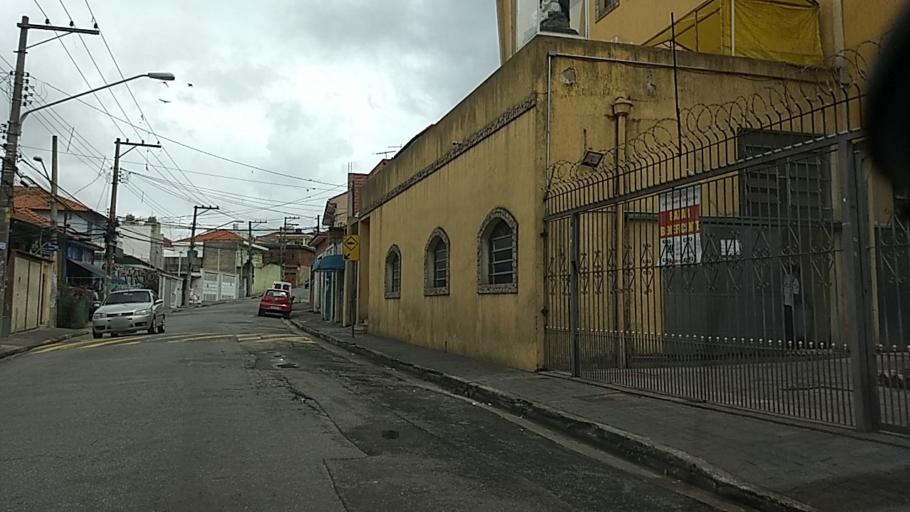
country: BR
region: Sao Paulo
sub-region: Guarulhos
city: Guarulhos
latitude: -23.4807
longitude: -46.5906
